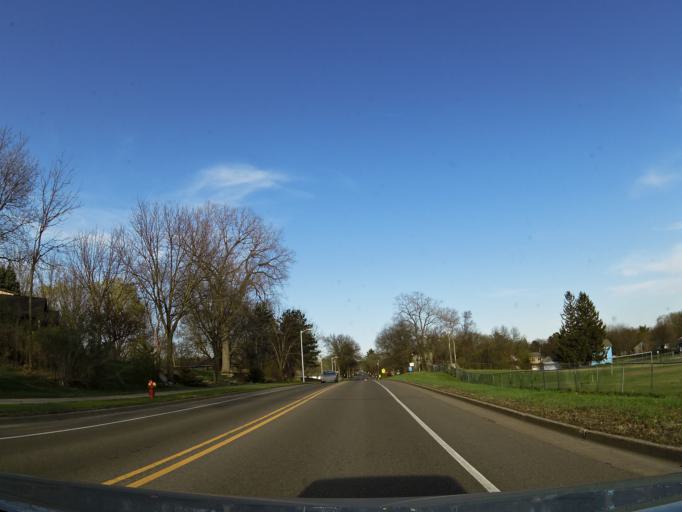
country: US
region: Wisconsin
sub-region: Pierce County
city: River Falls
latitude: 44.8626
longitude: -92.6387
